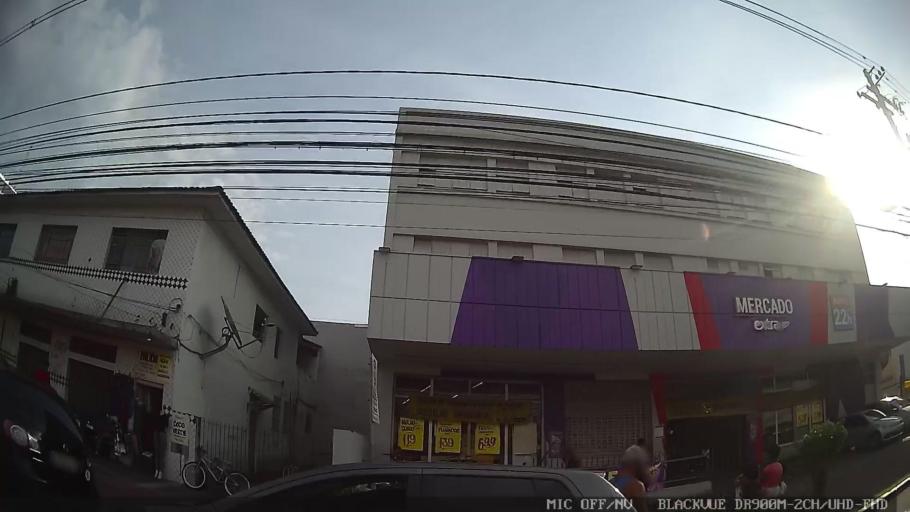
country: BR
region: Sao Paulo
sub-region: Cubatao
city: Cubatao
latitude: -23.8873
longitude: -46.4201
